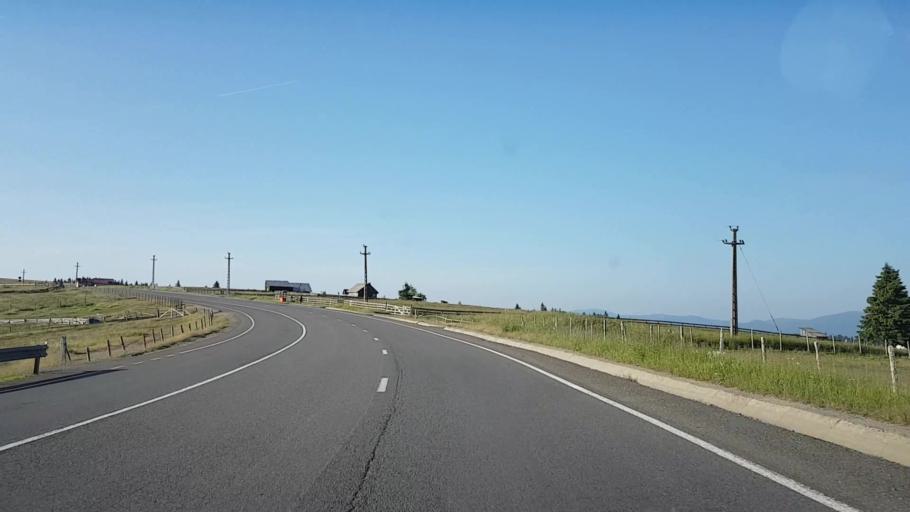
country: RO
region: Bistrita-Nasaud
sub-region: Comuna Lunca Ilvei
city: Lunca Ilvei
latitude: 47.2501
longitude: 25.0243
